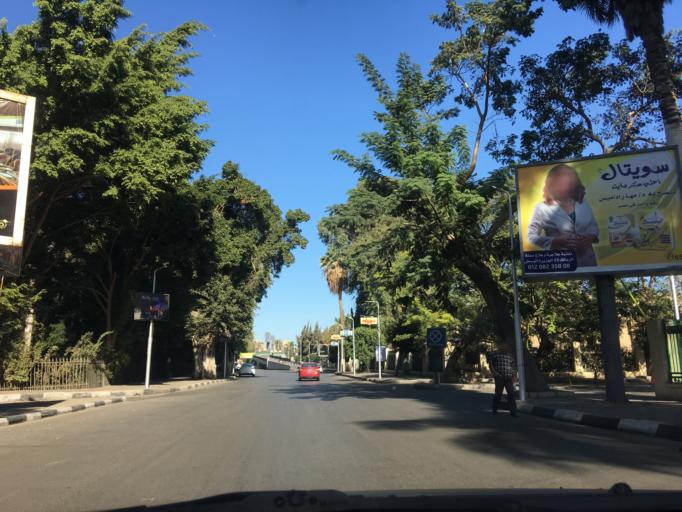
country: EG
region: Muhafazat al Qahirah
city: Cairo
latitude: 30.0456
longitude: 31.2271
